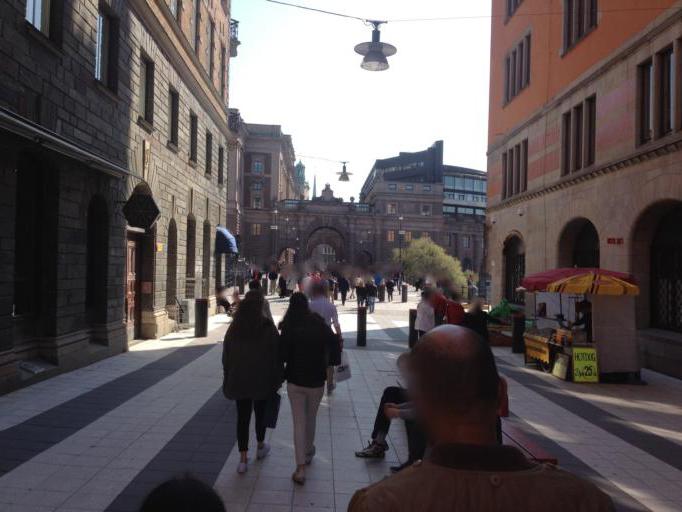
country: SE
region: Stockholm
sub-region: Stockholms Kommun
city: Stockholm
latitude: 59.3287
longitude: 18.0665
